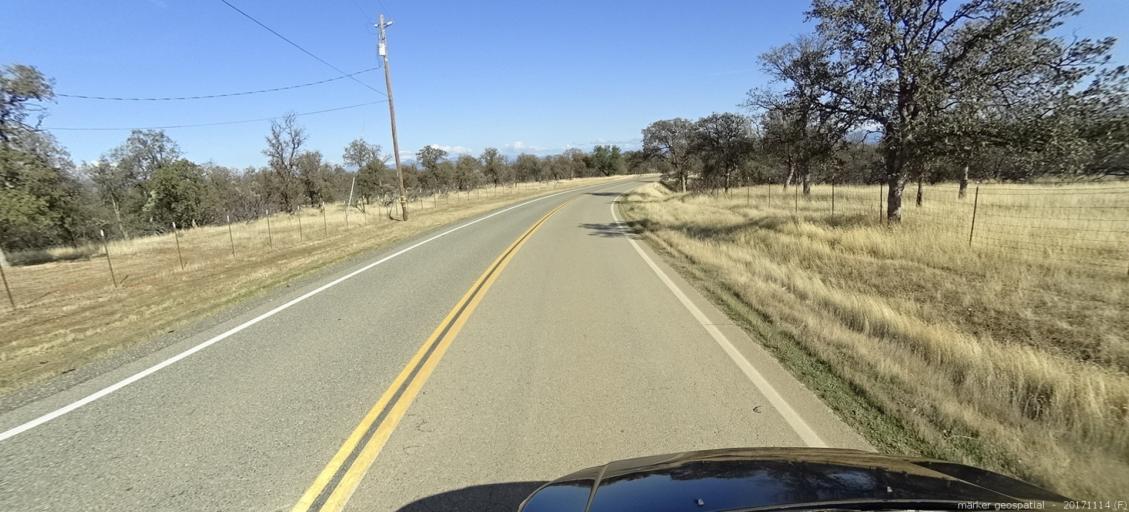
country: US
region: California
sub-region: Shasta County
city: Anderson
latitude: 40.4172
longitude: -122.3399
